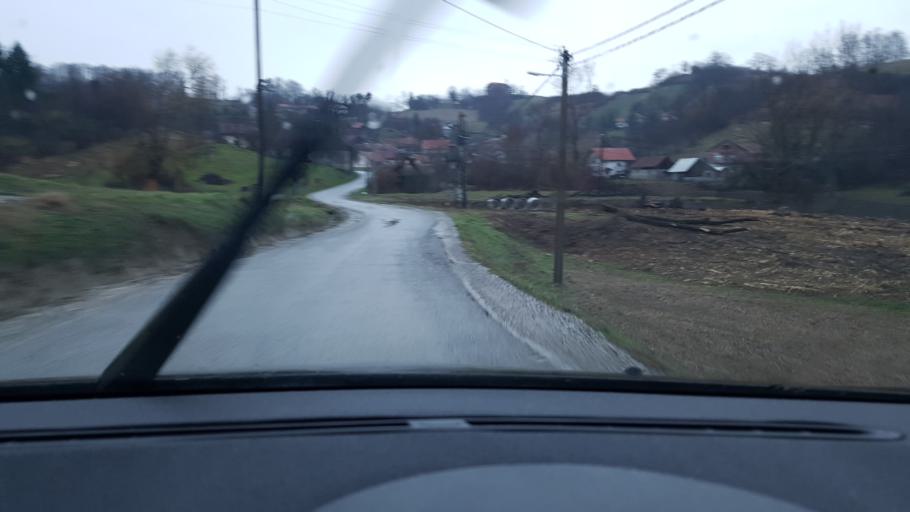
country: HR
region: Krapinsko-Zagorska
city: Bedekovcina
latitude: 45.9894
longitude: 15.9800
